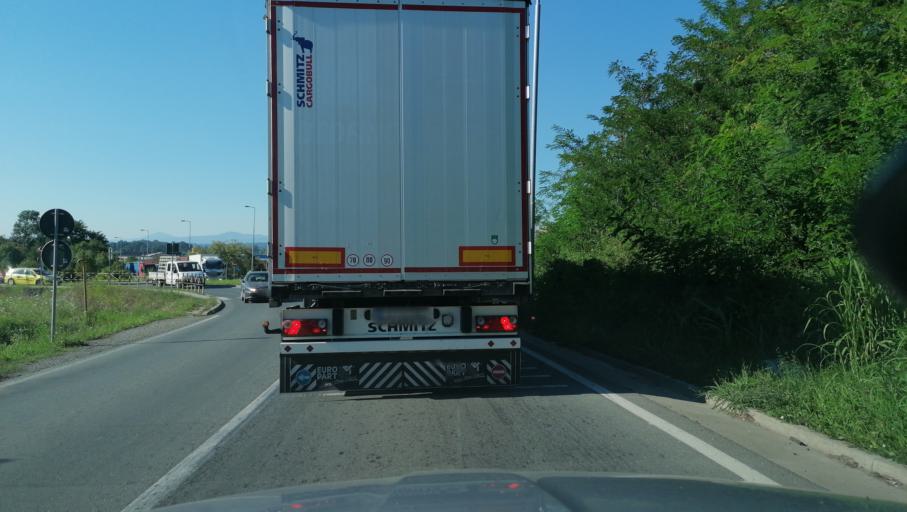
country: RS
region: Central Serbia
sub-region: Raski Okrug
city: Kraljevo
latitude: 43.7366
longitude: 20.6705
